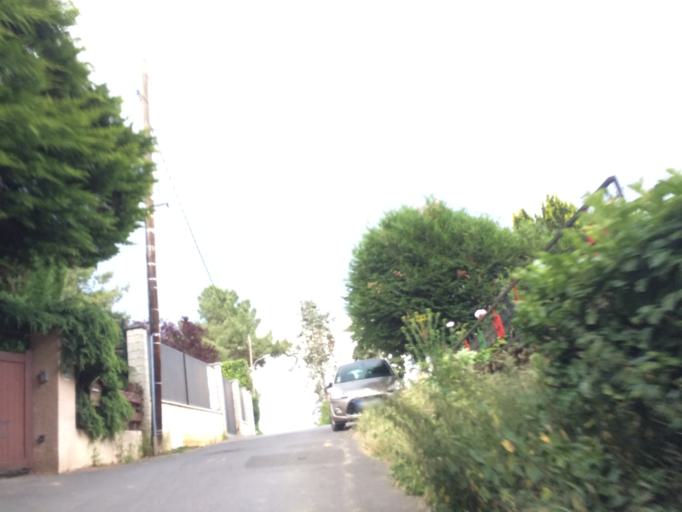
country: FR
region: Ile-de-France
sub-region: Departement des Hauts-de-Seine
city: Chatenay-Malabry
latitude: 48.7557
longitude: 2.2639
